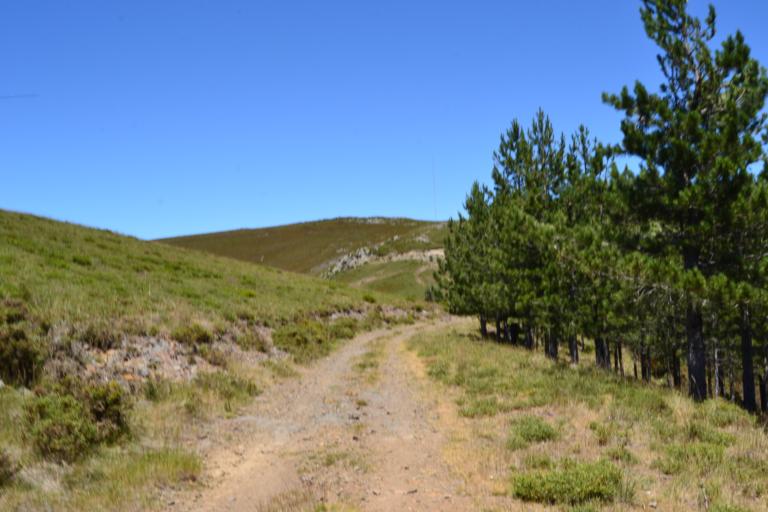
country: PT
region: Vila Real
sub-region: Mesao Frio
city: Mesao Frio
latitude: 41.2384
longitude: -7.9023
